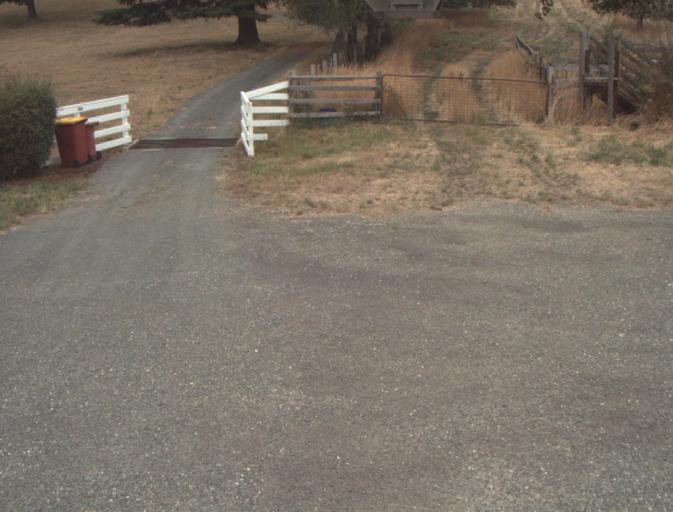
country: AU
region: Tasmania
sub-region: Launceston
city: Mayfield
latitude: -41.2587
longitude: 147.2180
